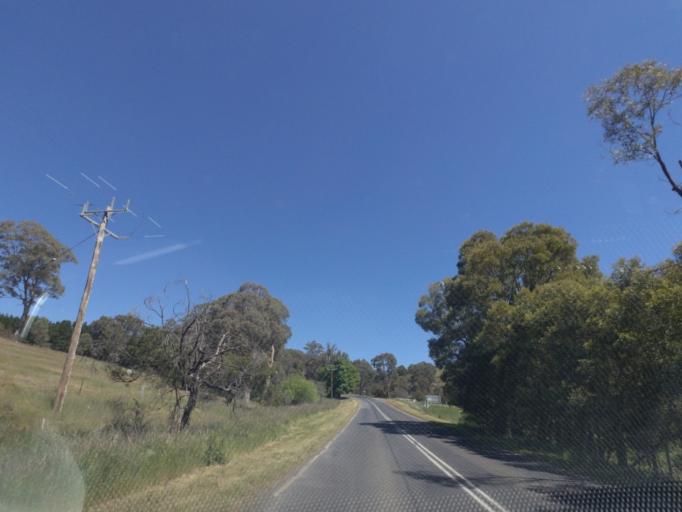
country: AU
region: Victoria
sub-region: Whittlesea
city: Whittlesea
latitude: -37.2884
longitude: 144.9773
